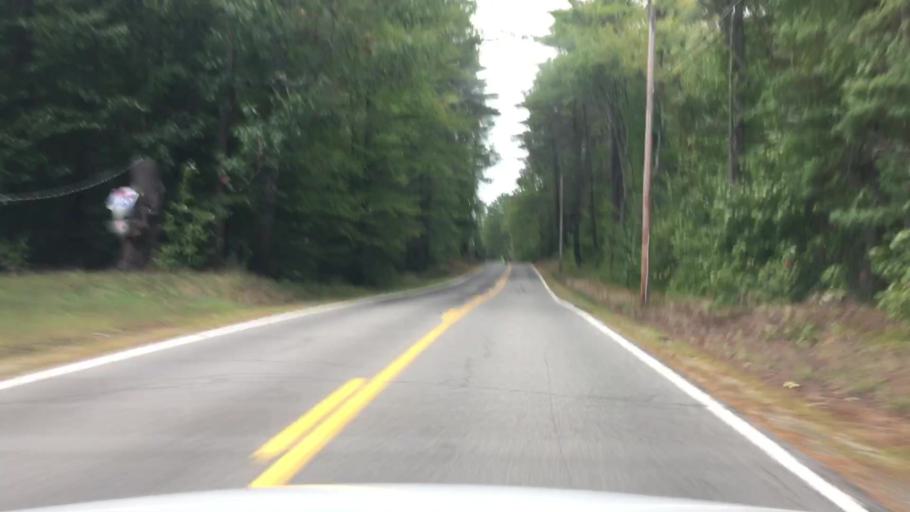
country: US
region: New Hampshire
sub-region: Carroll County
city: Effingham
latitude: 43.7164
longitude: -70.9902
